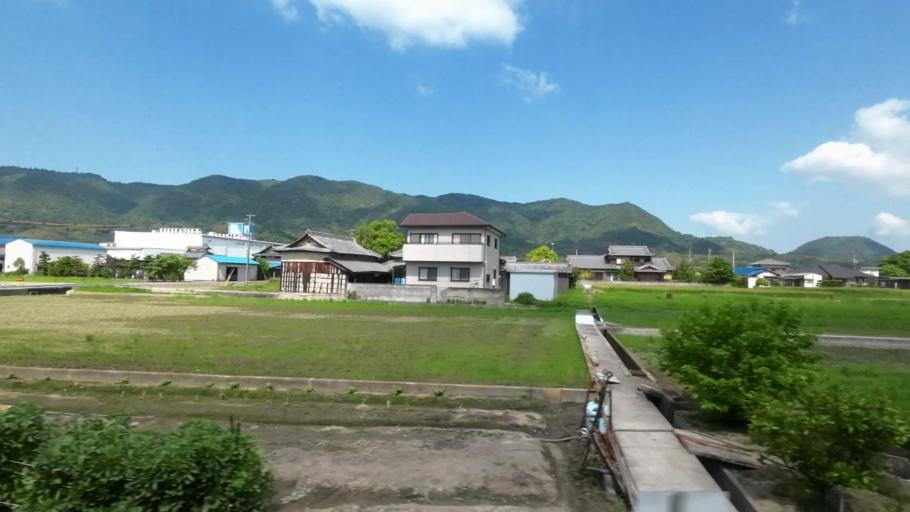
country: JP
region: Kagawa
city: Kan'onjicho
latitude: 34.1721
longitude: 133.6920
